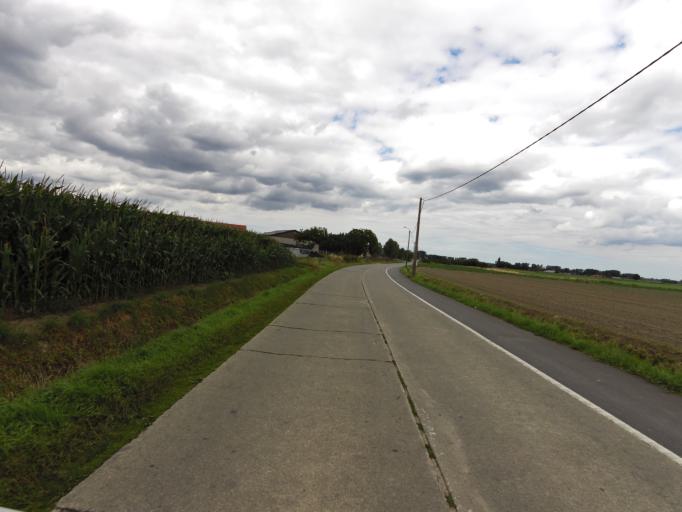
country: BE
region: Flanders
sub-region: Provincie West-Vlaanderen
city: Kortemark
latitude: 51.0064
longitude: 3.0516
